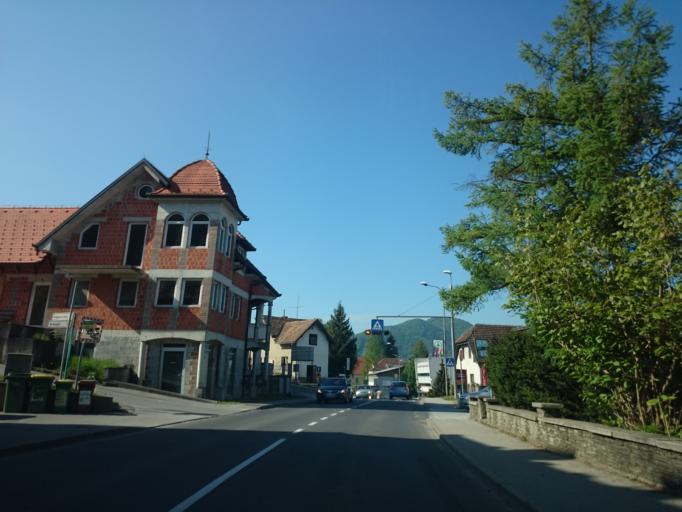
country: SI
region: Sentjur pri Celju
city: Sentjur
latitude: 46.2175
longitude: 15.3958
